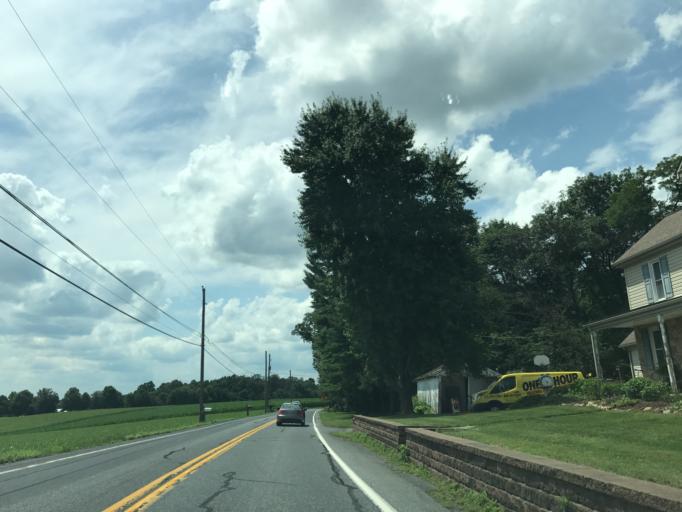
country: US
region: Pennsylvania
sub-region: Lancaster County
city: Brickerville
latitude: 40.2084
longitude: -76.3279
